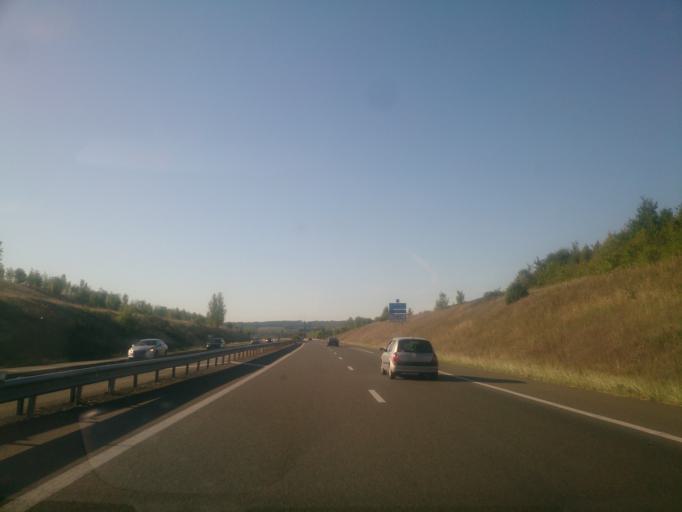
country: FR
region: Midi-Pyrenees
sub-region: Departement du Tarn-et-Garonne
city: Caussade
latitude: 44.2261
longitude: 1.5355
